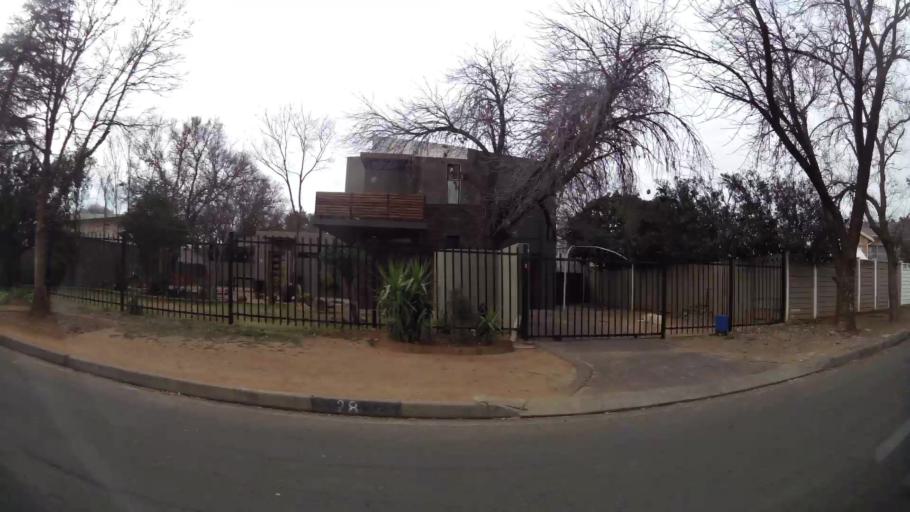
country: ZA
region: Orange Free State
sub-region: Mangaung Metropolitan Municipality
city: Bloemfontein
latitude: -29.1222
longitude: 26.1940
